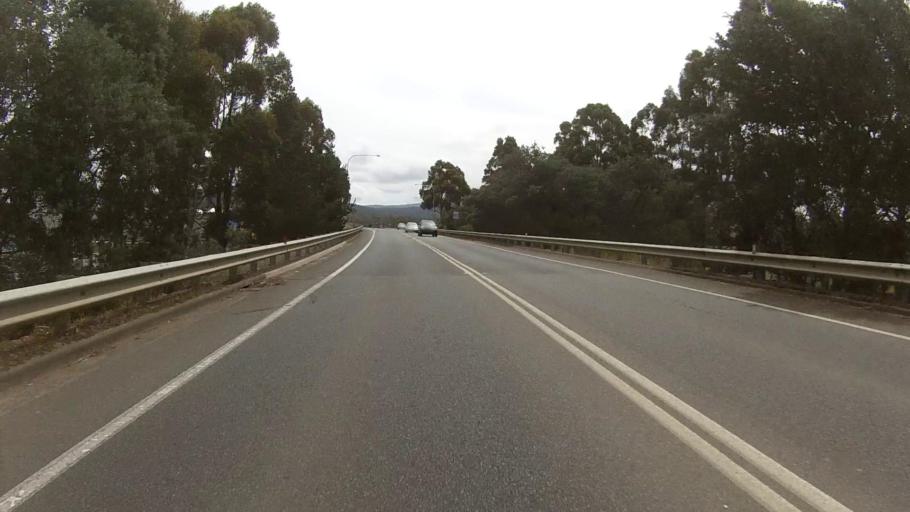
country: AU
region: Tasmania
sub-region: Kingborough
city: Kingston
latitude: -42.9884
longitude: 147.2924
